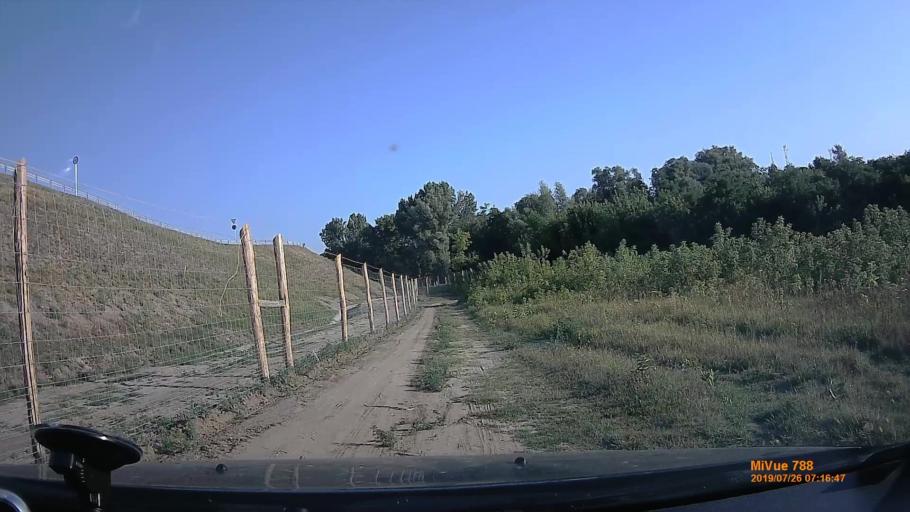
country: HU
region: Pest
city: Mogyorod
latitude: 47.5930
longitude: 19.2305
